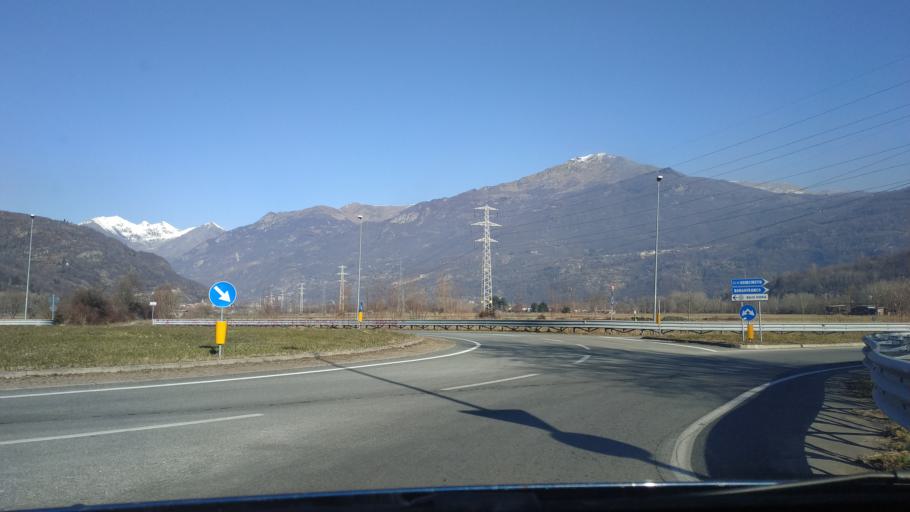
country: IT
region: Piedmont
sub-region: Provincia di Torino
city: Quassolo
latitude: 45.5078
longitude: 7.8356
